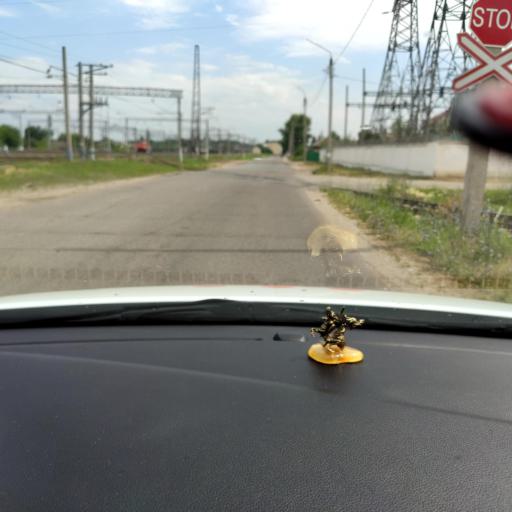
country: RU
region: Tatarstan
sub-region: Zelenodol'skiy Rayon
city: Zelenodolsk
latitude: 55.8413
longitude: 48.5509
